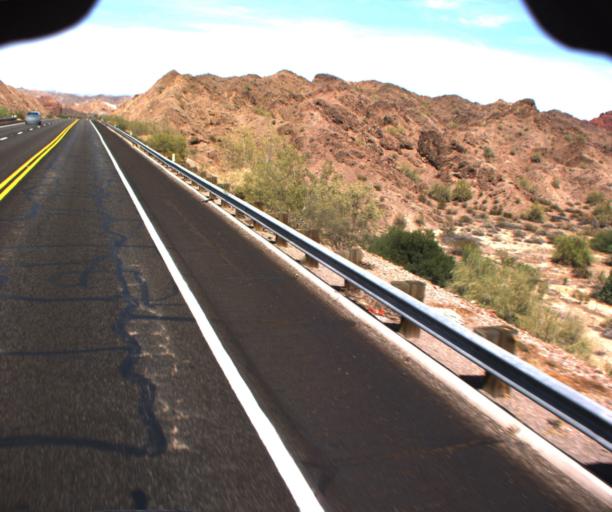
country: US
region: Arizona
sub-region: La Paz County
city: Cienega Springs
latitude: 34.2322
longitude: -114.1795
